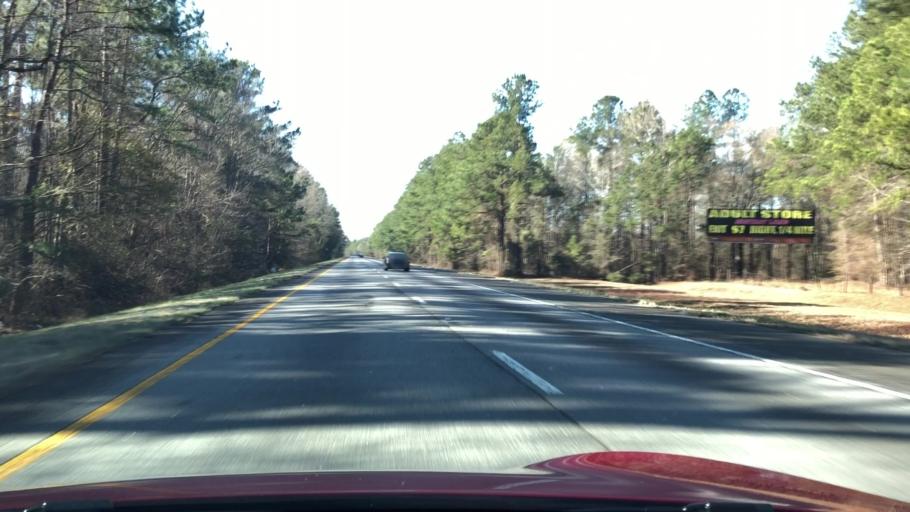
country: US
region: South Carolina
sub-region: Clarendon County
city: Manning
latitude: 33.5599
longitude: -80.3978
